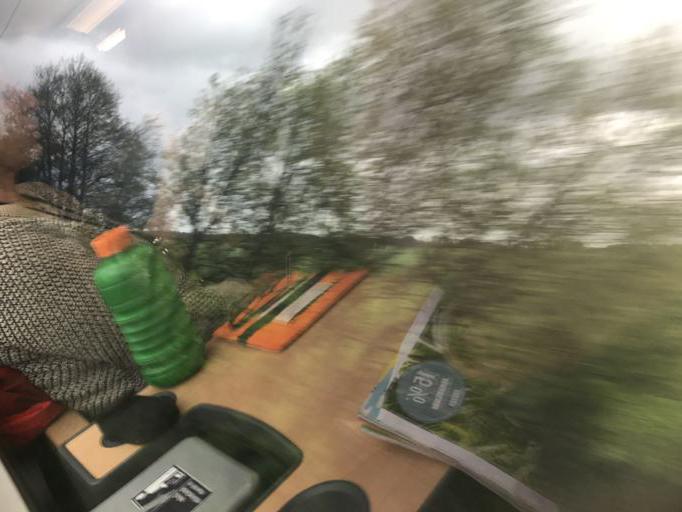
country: DE
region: Schleswig-Holstein
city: Wulfsmoor
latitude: 53.9143
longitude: 9.7327
